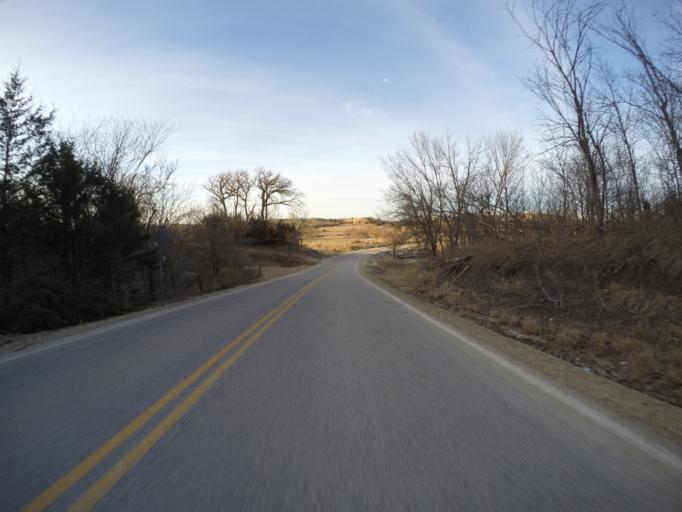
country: US
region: Kansas
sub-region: Riley County
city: Manhattan
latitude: 39.2939
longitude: -96.7011
